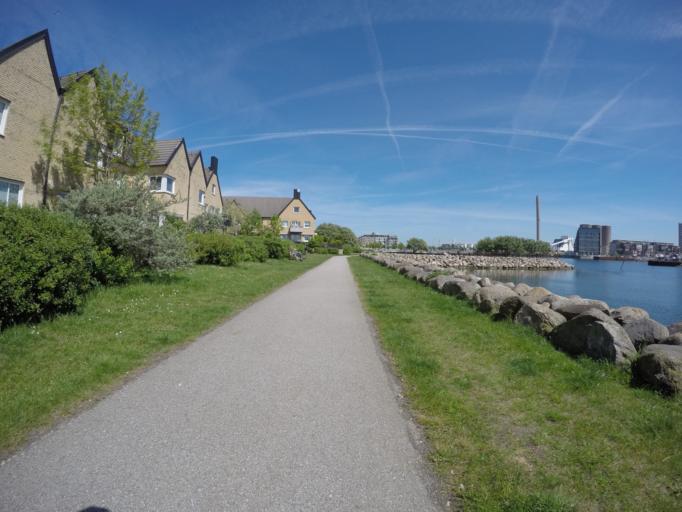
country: SE
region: Skane
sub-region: Malmo
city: Bunkeflostrand
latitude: 55.5869
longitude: 12.9194
